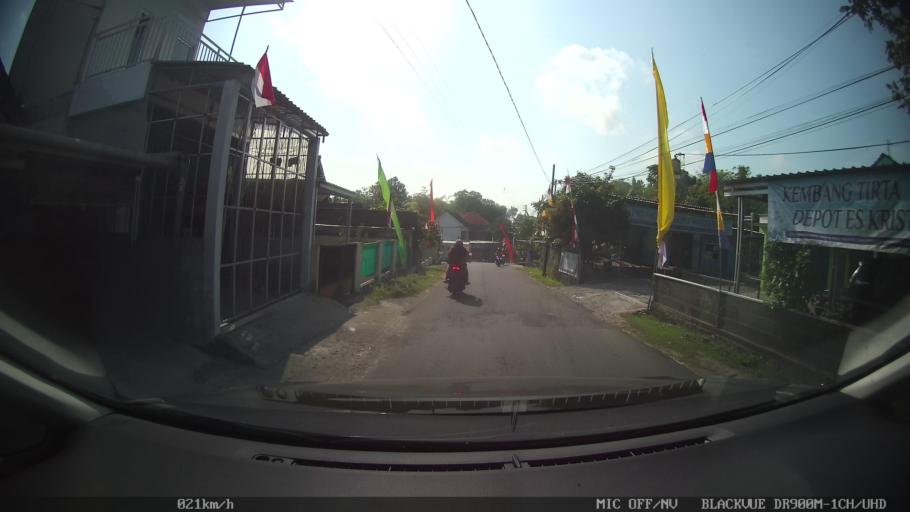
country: ID
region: Daerah Istimewa Yogyakarta
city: Gamping Lor
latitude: -7.8132
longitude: 110.2987
